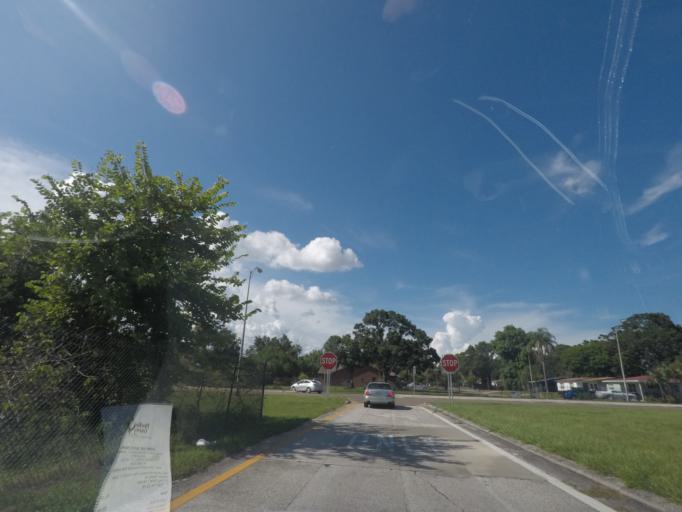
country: US
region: Florida
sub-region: Pinellas County
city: Saint Petersburg
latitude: 27.7444
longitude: -82.6765
